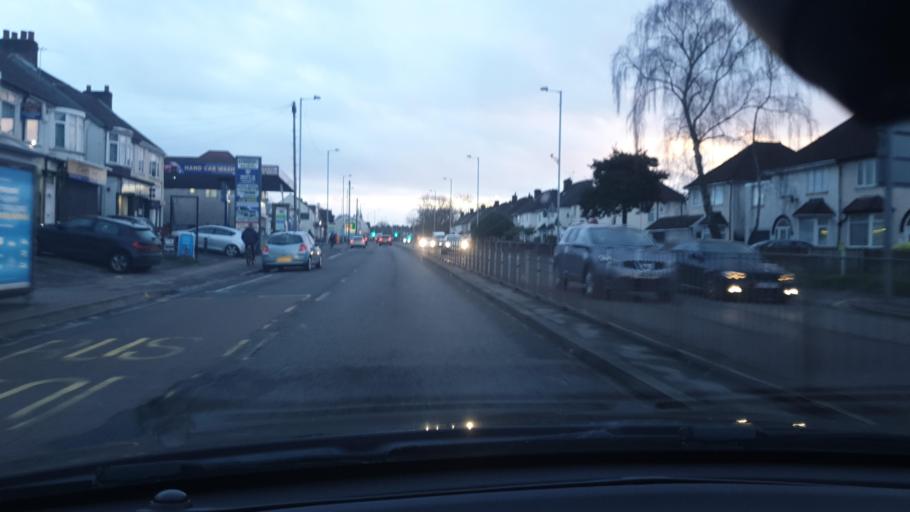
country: GB
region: England
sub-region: Wolverhampton
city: Wolverhampton
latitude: 52.6203
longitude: -2.1298
